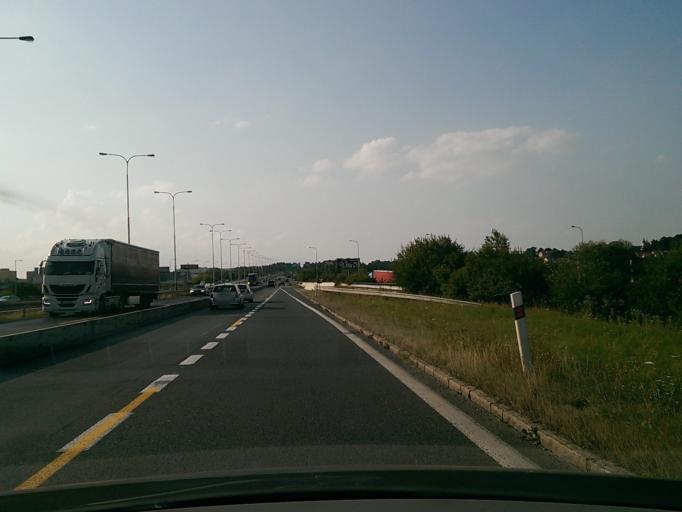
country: CZ
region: Praha
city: Cerny Most
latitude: 50.1004
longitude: 14.5920
